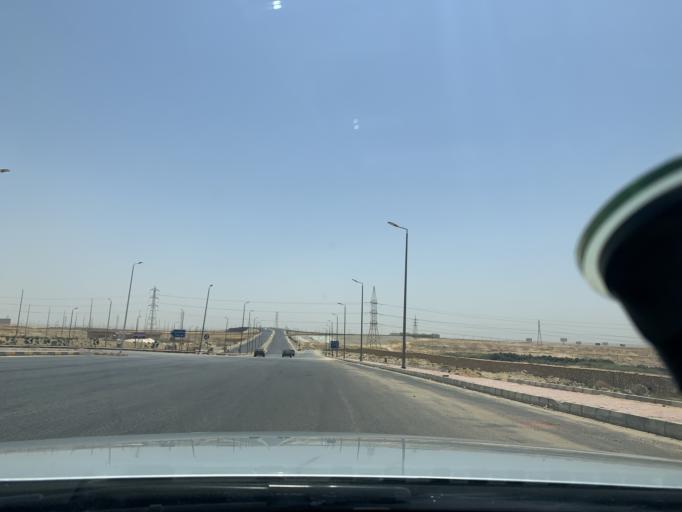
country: EG
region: Muhafazat al Qahirah
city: Halwan
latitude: 29.9757
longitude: 31.4703
